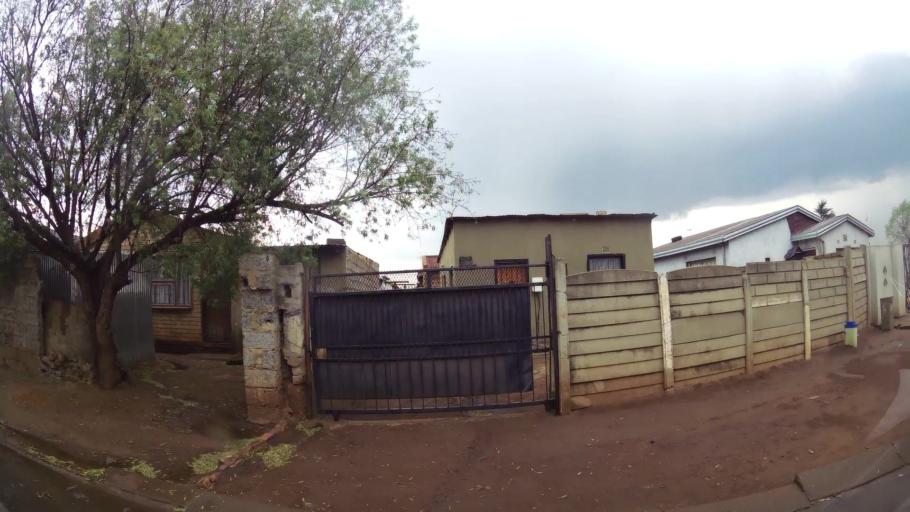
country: ZA
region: Gauteng
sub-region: Ekurhuleni Metropolitan Municipality
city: Germiston
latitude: -26.3649
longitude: 28.1402
